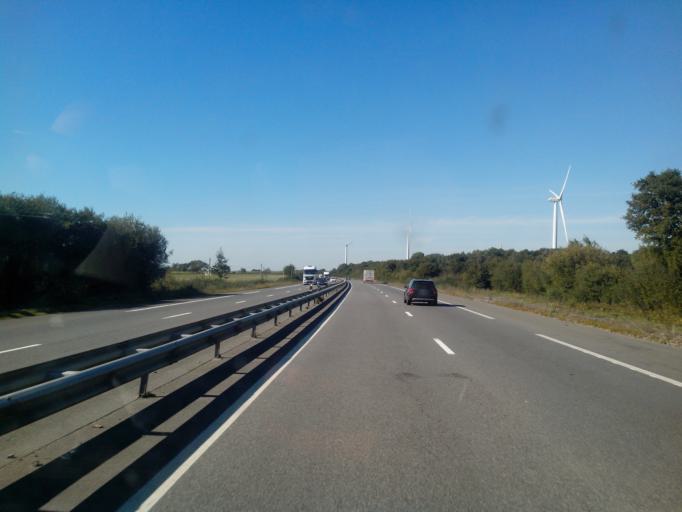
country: FR
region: Pays de la Loire
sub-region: Departement de la Loire-Atlantique
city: Prinquiau
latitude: 47.4056
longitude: -2.0118
